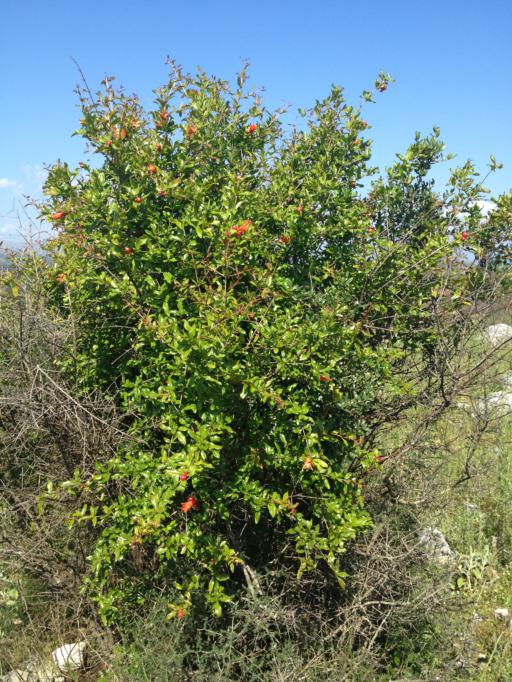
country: AL
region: Shkoder
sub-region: Rrethi i Shkodres
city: Dajc
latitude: 41.9885
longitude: 19.3174
